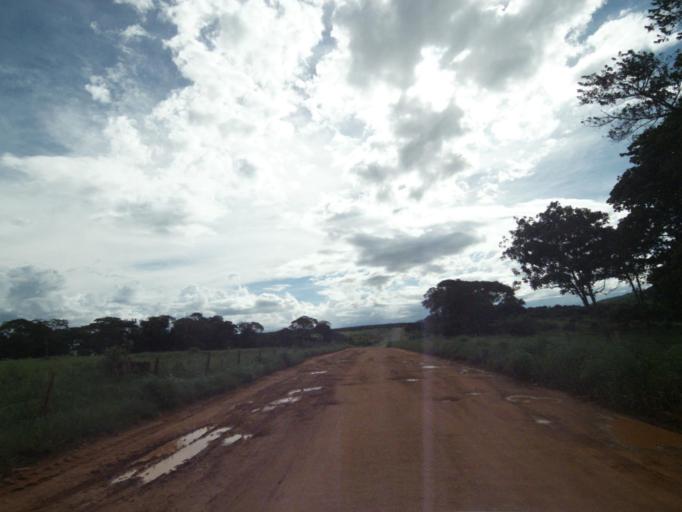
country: BR
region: Goias
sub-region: Jaragua
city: Jaragua
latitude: -15.8369
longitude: -49.2768
